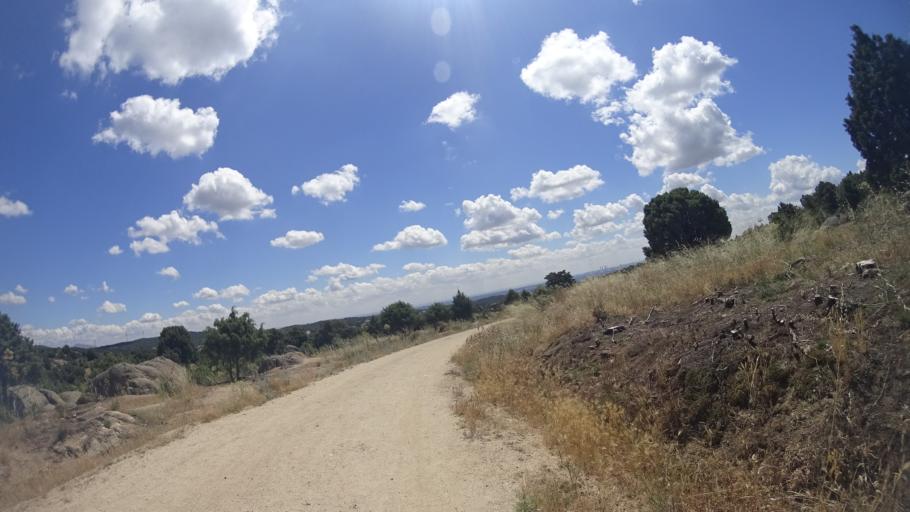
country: ES
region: Madrid
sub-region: Provincia de Madrid
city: Hoyo de Manzanares
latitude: 40.6023
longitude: -3.9164
